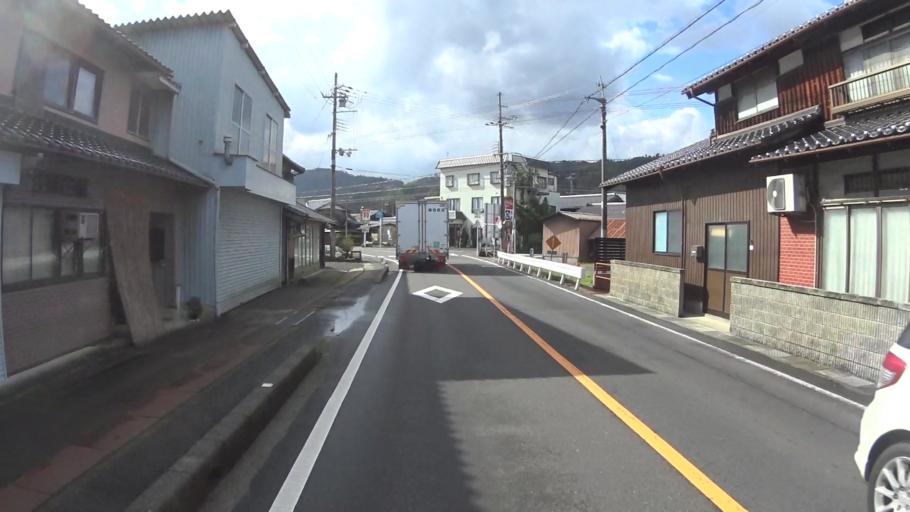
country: JP
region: Kyoto
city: Miyazu
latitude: 35.5707
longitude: 135.1569
